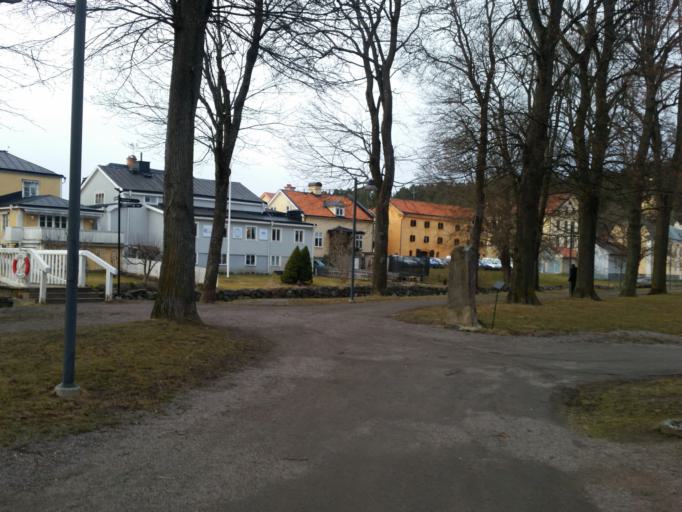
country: SE
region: OEstergoetland
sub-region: Soderkopings Kommun
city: Soederkoeping
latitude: 58.4803
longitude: 16.3194
